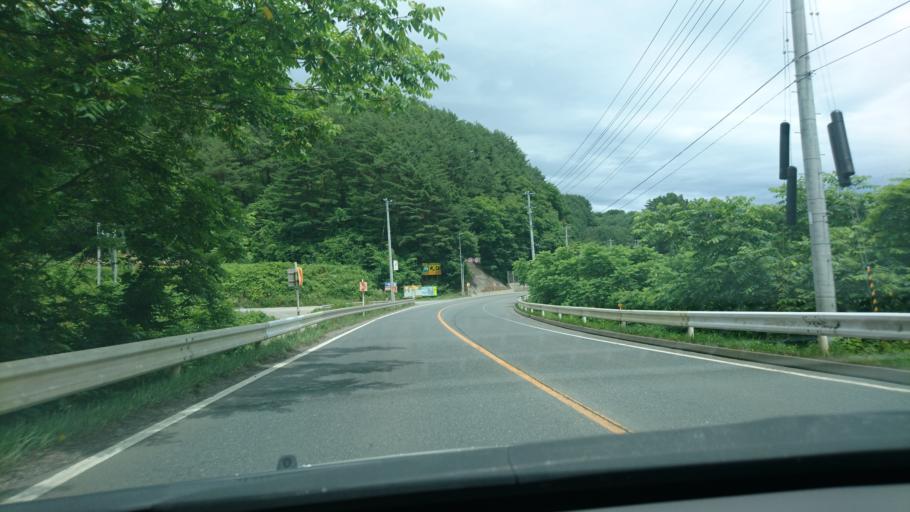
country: JP
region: Iwate
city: Miyako
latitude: 39.7026
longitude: 141.9553
